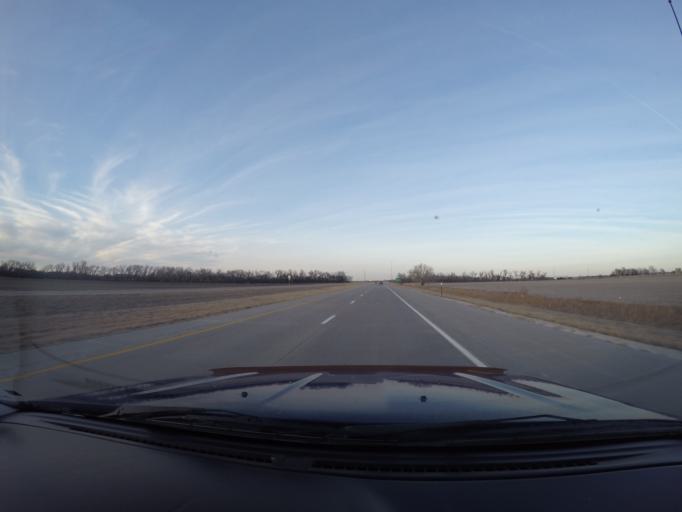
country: US
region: Kansas
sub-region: Saline County
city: Salina
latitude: 38.7326
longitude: -97.6181
